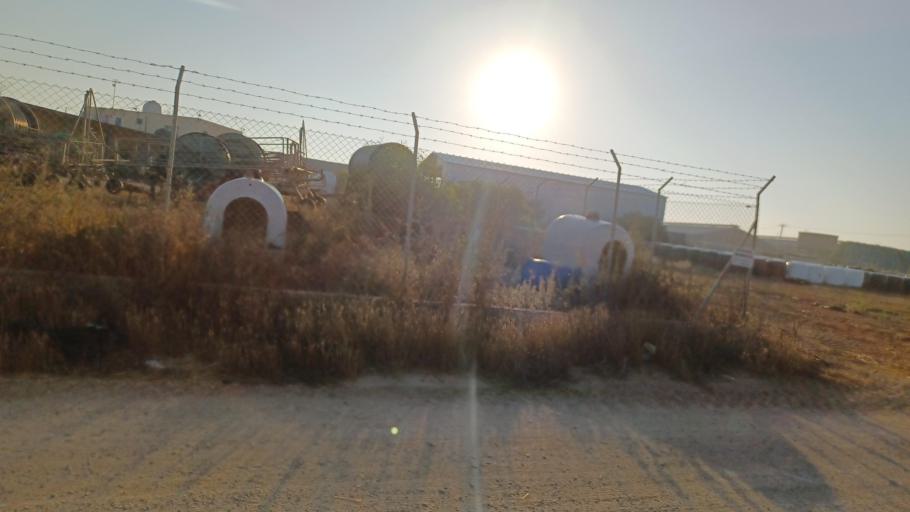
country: CY
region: Ammochostos
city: Achna
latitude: 35.0184
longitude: 33.7990
